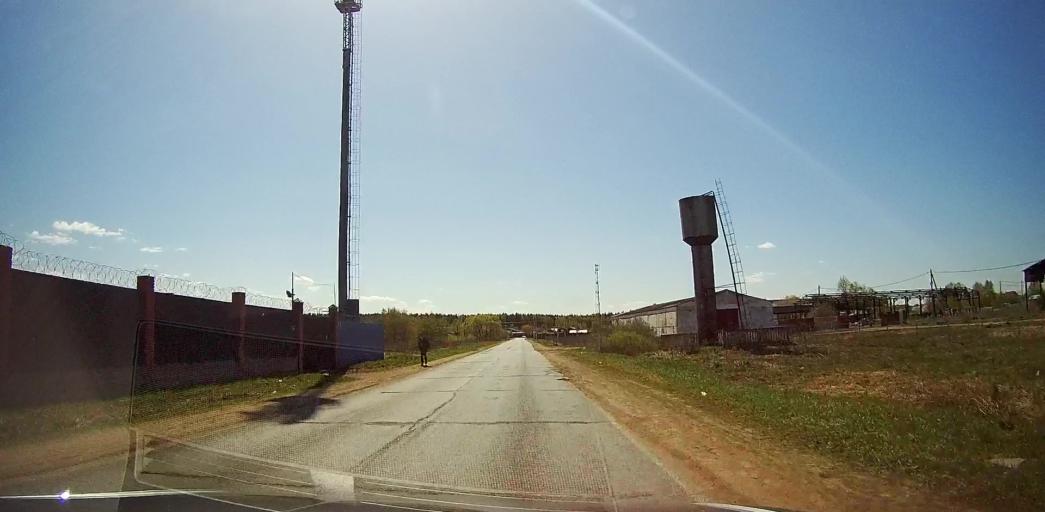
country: RU
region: Moskovskaya
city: Bronnitsy
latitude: 55.4577
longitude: 38.3043
